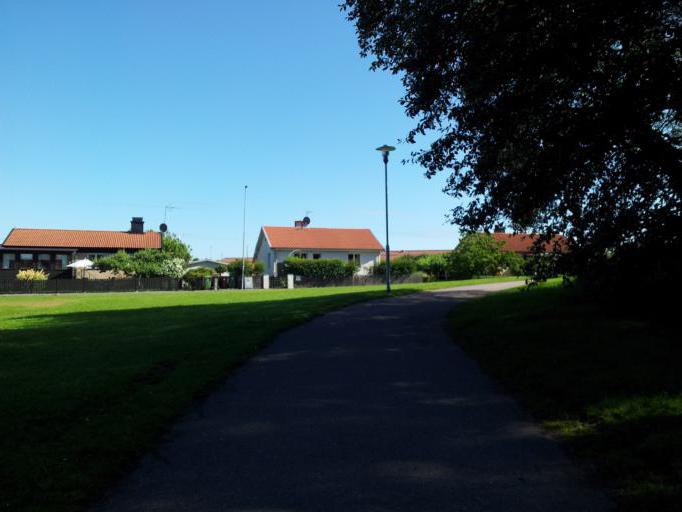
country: SE
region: Uppsala
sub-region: Uppsala Kommun
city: Uppsala
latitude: 59.8600
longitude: 17.6709
